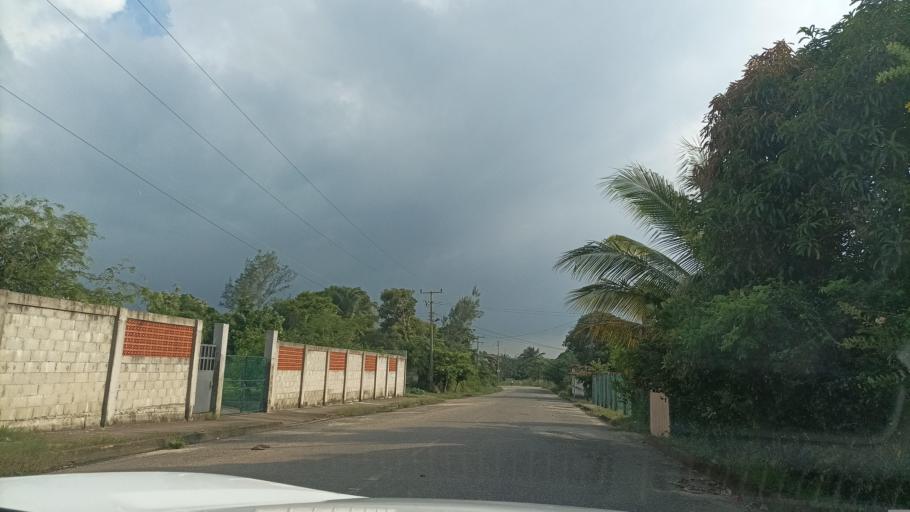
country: MX
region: Veracruz
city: Allende
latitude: 18.1570
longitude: -94.3249
